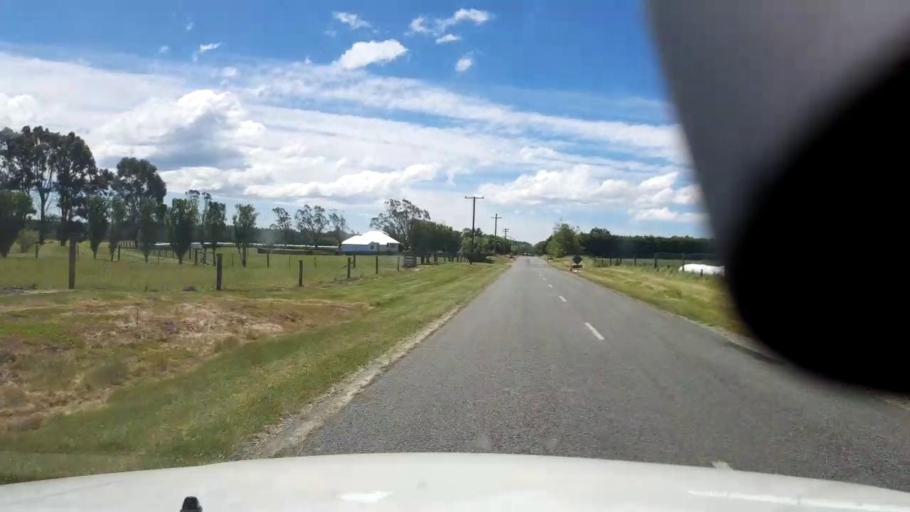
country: NZ
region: Canterbury
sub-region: Timaru District
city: Pleasant Point
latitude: -44.2744
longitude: 171.2532
